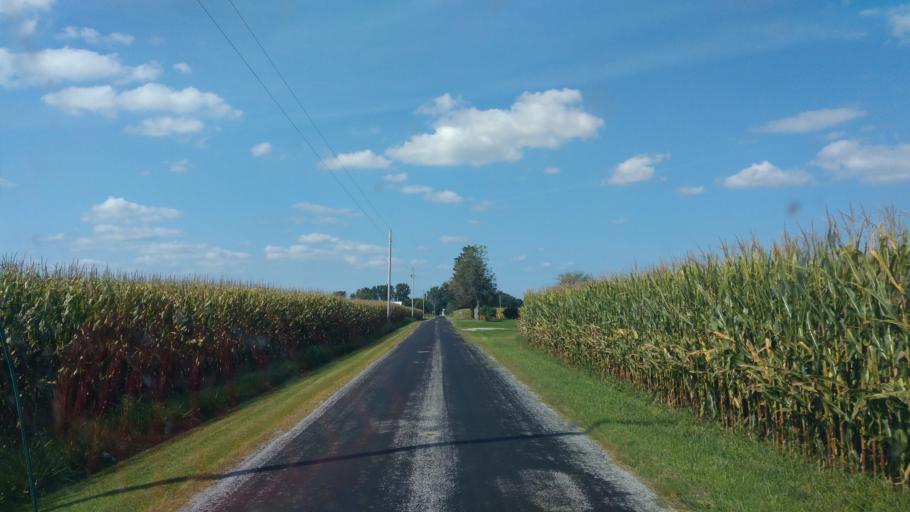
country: US
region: Ohio
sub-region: Hardin County
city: Forest
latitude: 40.7057
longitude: -83.4778
